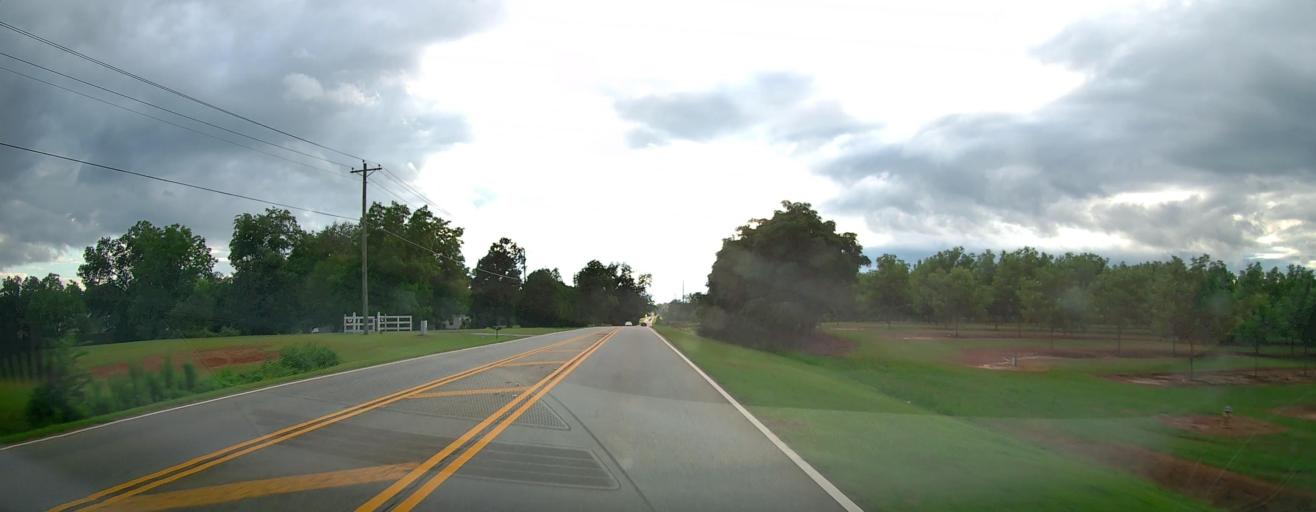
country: US
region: Georgia
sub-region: Houston County
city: Perry
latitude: 32.4546
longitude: -83.6949
